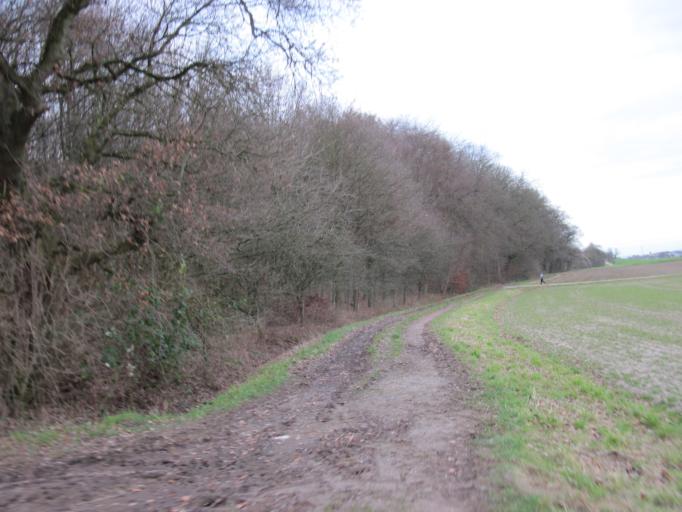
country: DE
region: North Rhine-Westphalia
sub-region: Regierungsbezirk Detmold
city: Paderborn
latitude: 51.7018
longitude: 8.6902
